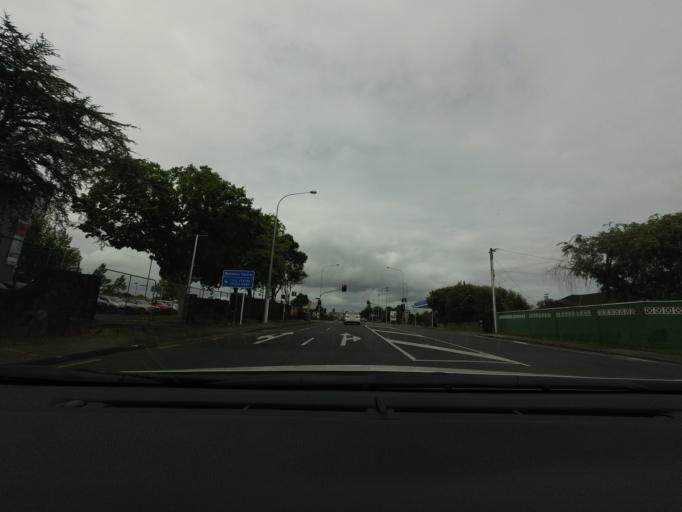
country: NZ
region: Auckland
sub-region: Auckland
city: Rosebank
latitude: -36.8806
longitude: 174.6292
